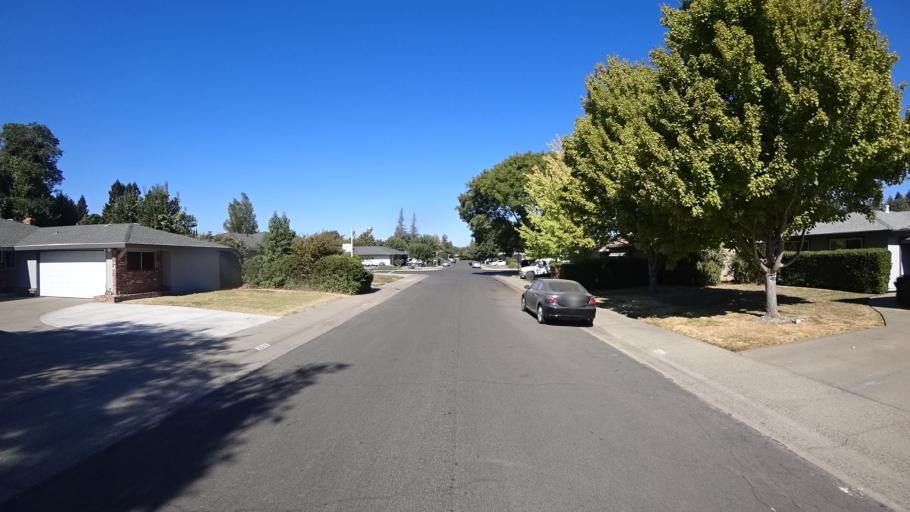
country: US
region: California
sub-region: Sacramento County
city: Parkway
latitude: 38.4989
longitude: -121.5205
